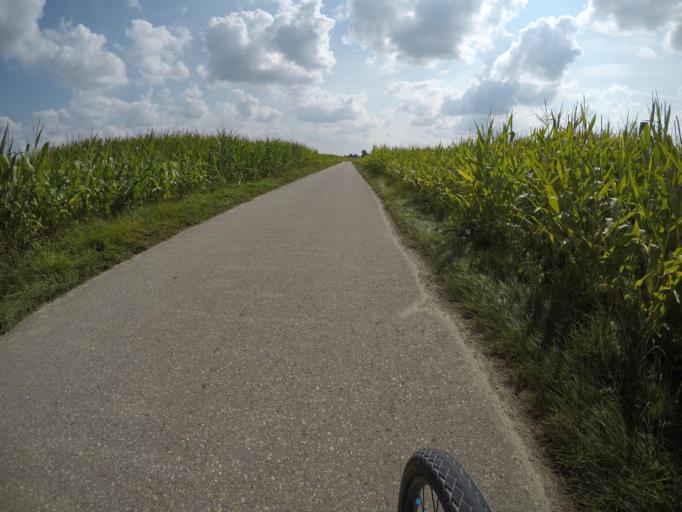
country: DE
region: Bavaria
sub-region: Swabia
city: Nordendorf
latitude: 48.5861
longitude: 10.8353
